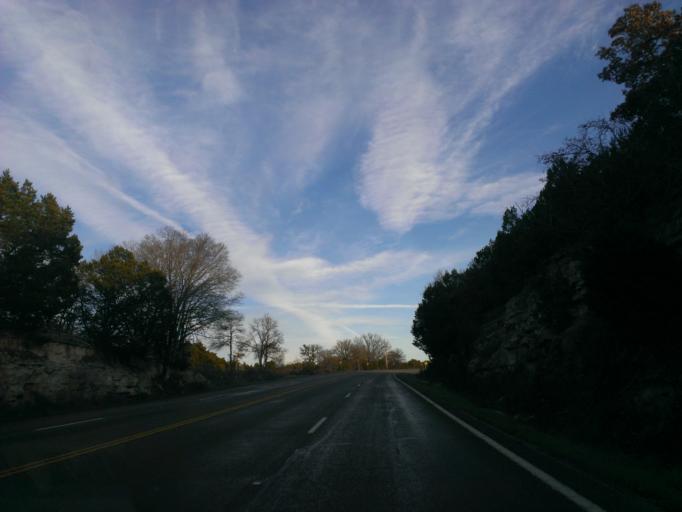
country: US
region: Texas
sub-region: Lampasas County
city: Kempner
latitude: 30.9271
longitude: -97.9925
